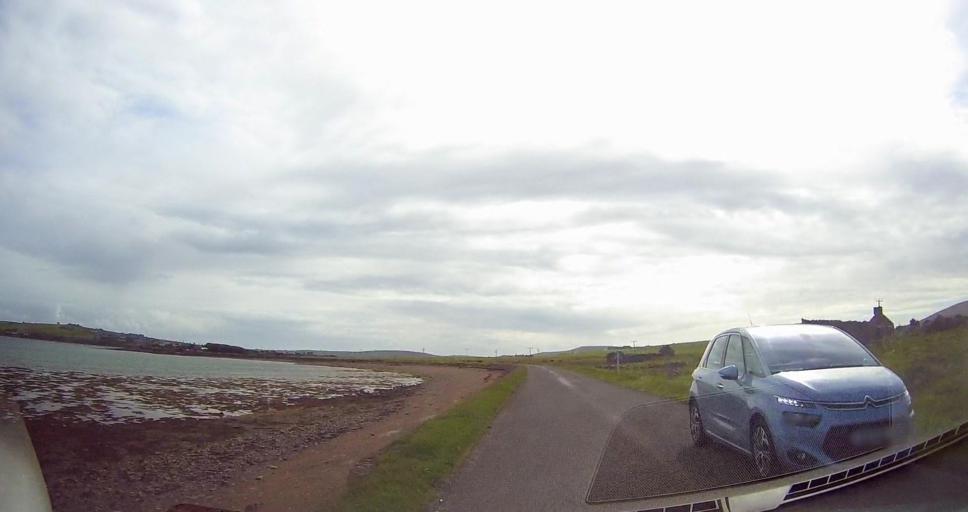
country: GB
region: Scotland
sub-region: Orkney Islands
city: Stromness
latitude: 58.8115
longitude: -3.2001
